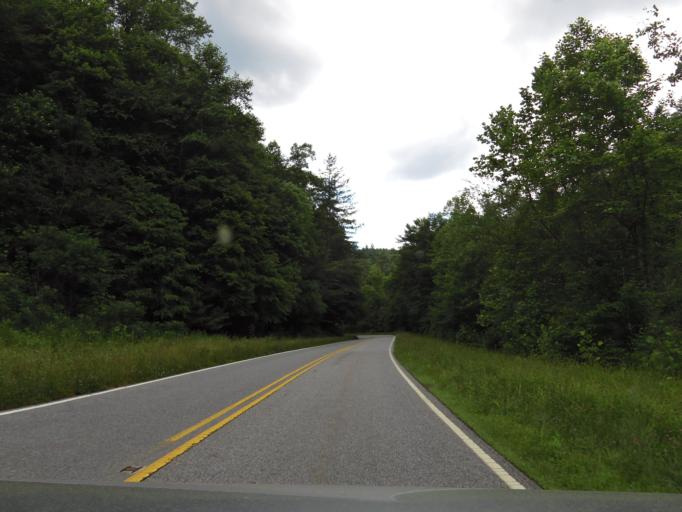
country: US
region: North Carolina
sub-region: Graham County
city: Robbinsville
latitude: 35.4053
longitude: -83.8851
